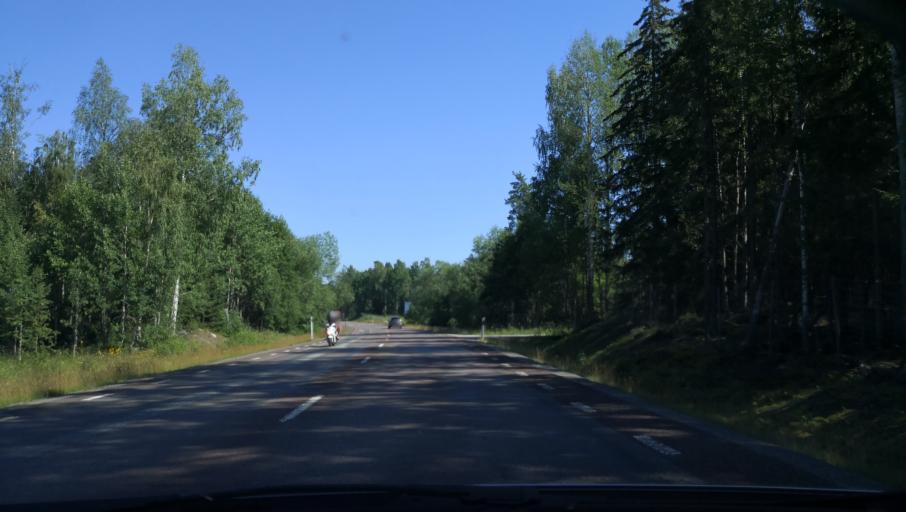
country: SE
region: Gaevleborg
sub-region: Ovanakers Kommun
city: Alfta
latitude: 61.3368
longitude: 16.0405
